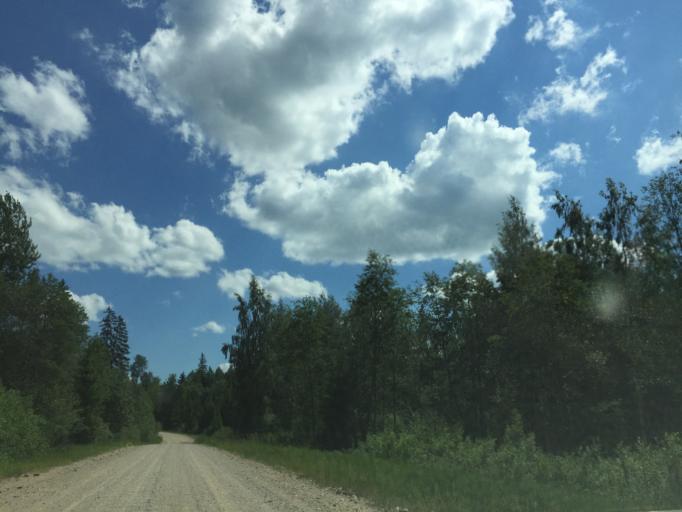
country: LV
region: Priekuli
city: Priekuli
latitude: 57.2500
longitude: 25.4334
